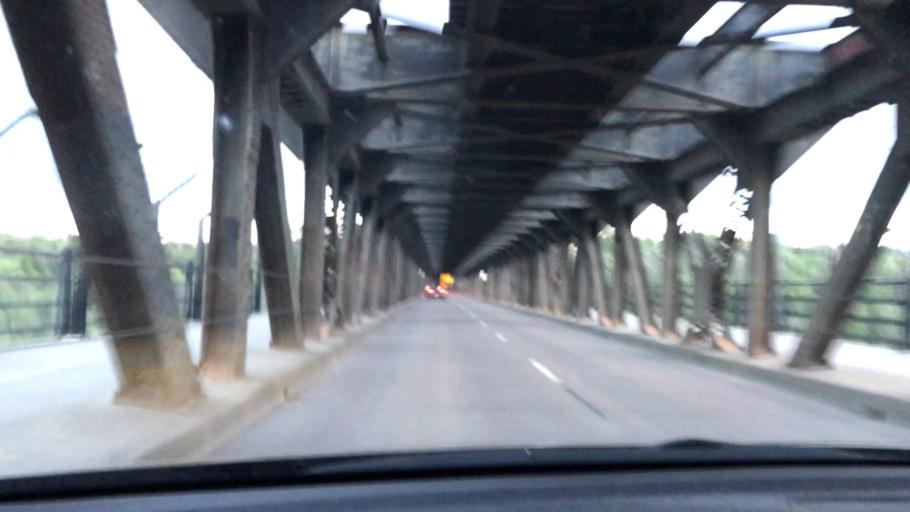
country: CA
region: Alberta
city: Edmonton
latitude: 53.5282
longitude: -113.5121
